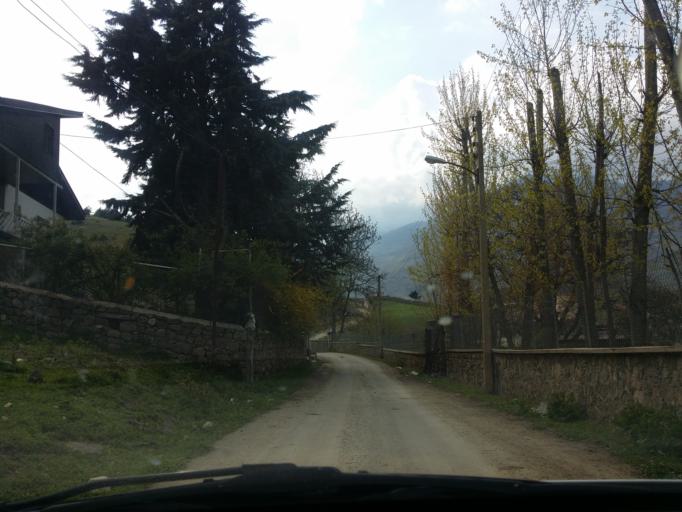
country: IR
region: Mazandaran
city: `Abbasabad
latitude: 36.4809
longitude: 51.1388
